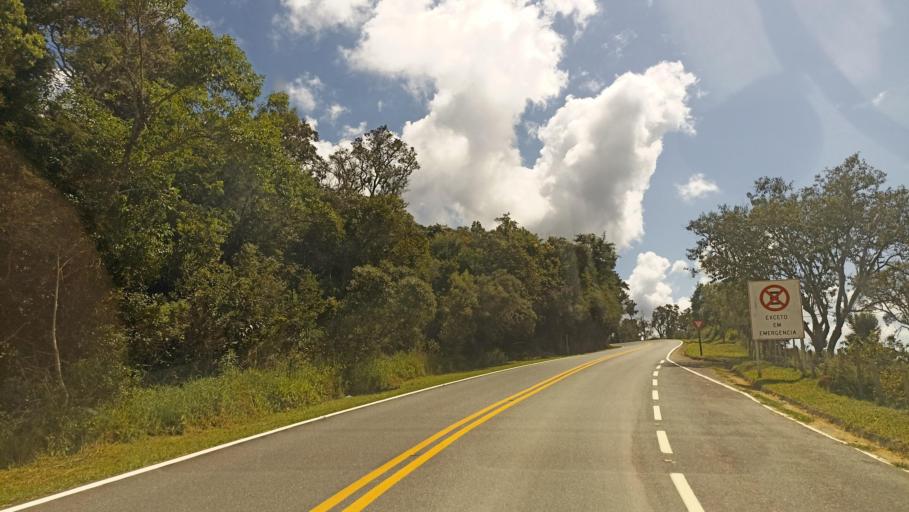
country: BR
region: Sao Paulo
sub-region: Cunha
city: Cunha
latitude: -23.1412
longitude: -44.8963
